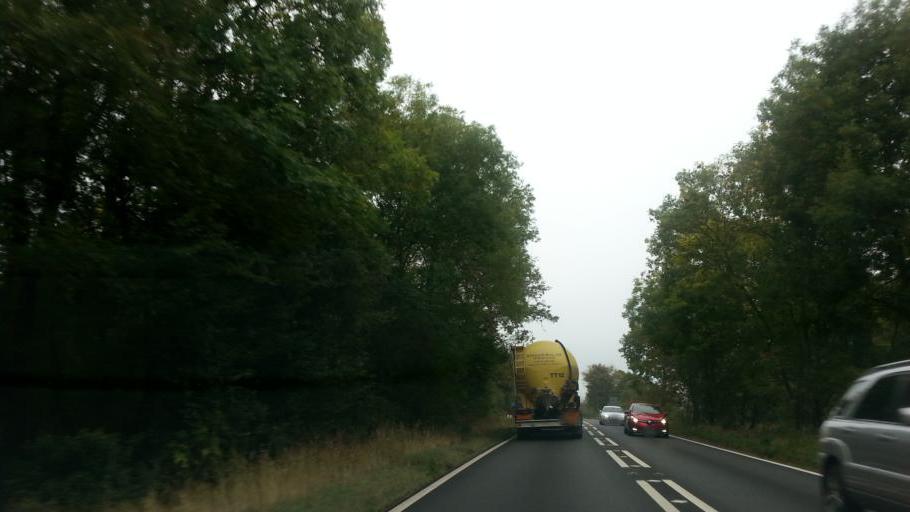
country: GB
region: England
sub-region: Northamptonshire
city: Oundle
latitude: 52.4399
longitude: -0.4729
